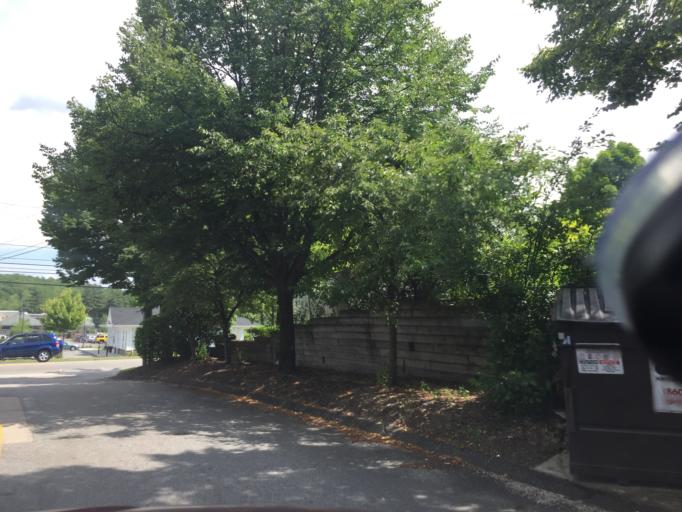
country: US
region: Connecticut
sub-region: Litchfield County
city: Torrington
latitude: 41.8258
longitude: -73.1139
